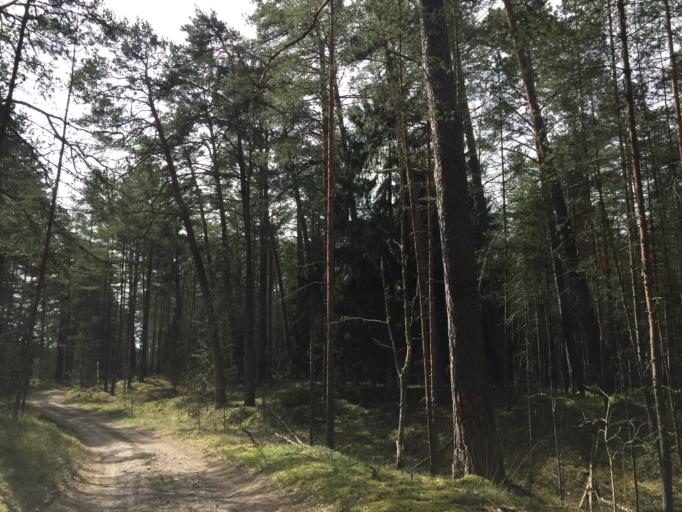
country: LV
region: Salacgrivas
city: Salacgriva
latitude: 57.6892
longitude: 24.3609
